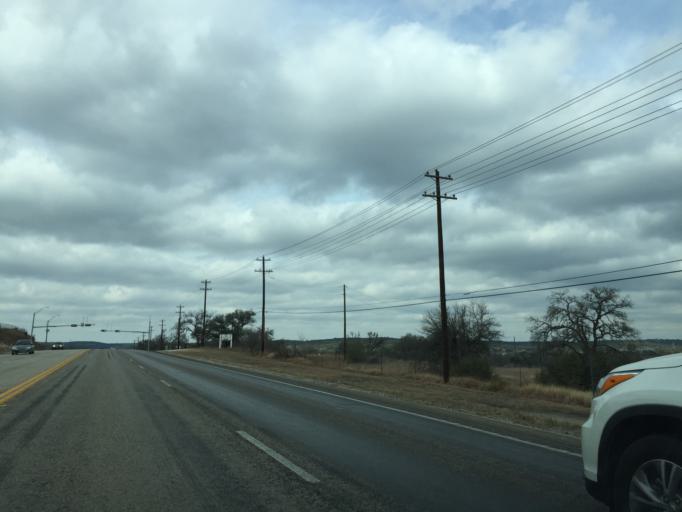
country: US
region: Texas
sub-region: Travis County
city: Briarcliff
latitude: 30.4077
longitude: -98.1055
